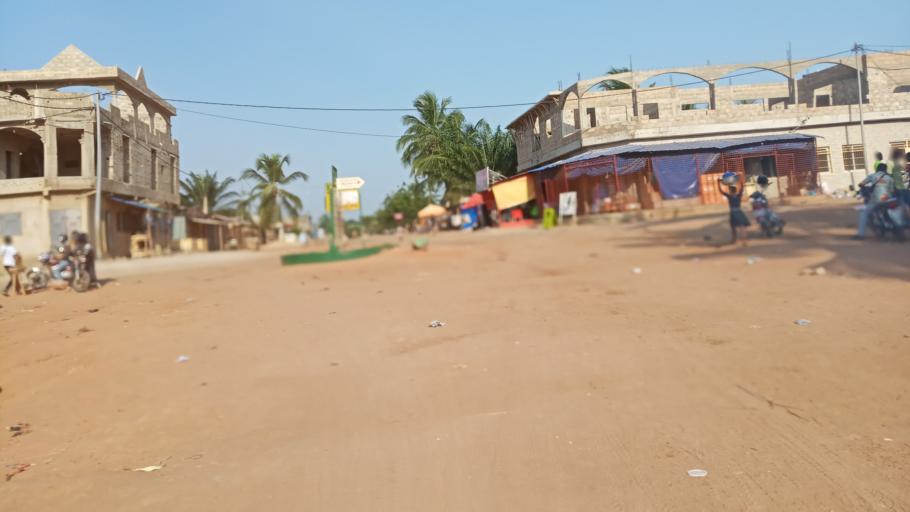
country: TG
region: Maritime
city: Lome
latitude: 6.1747
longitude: 1.1522
